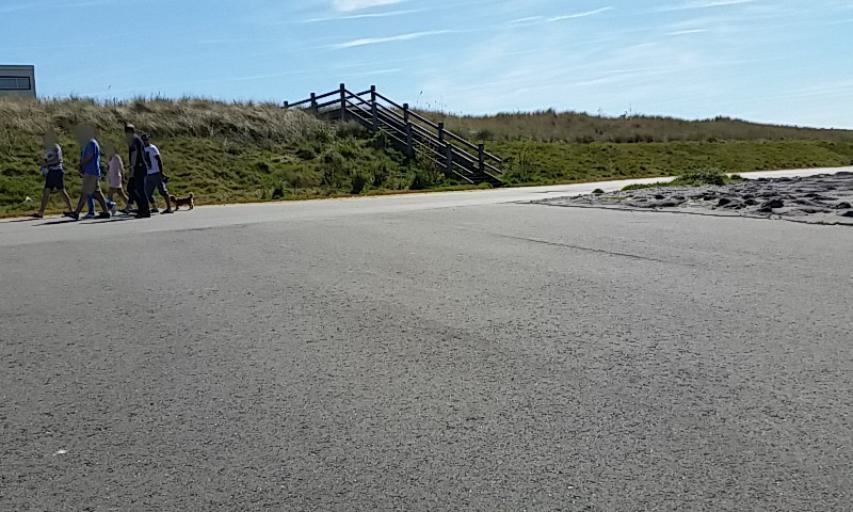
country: NL
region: Zeeland
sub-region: Gemeente Vlissingen
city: Vlissingen
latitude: 51.4010
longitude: 3.5517
